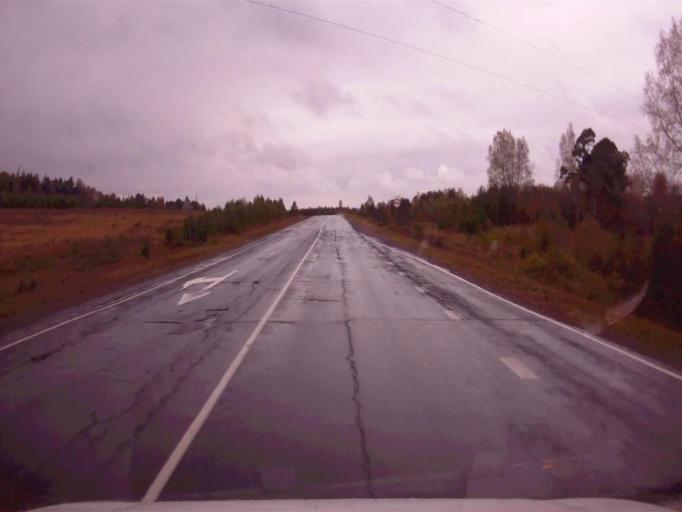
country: RU
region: Chelyabinsk
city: Verkhniy Ufaley
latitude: 56.0067
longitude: 60.3260
